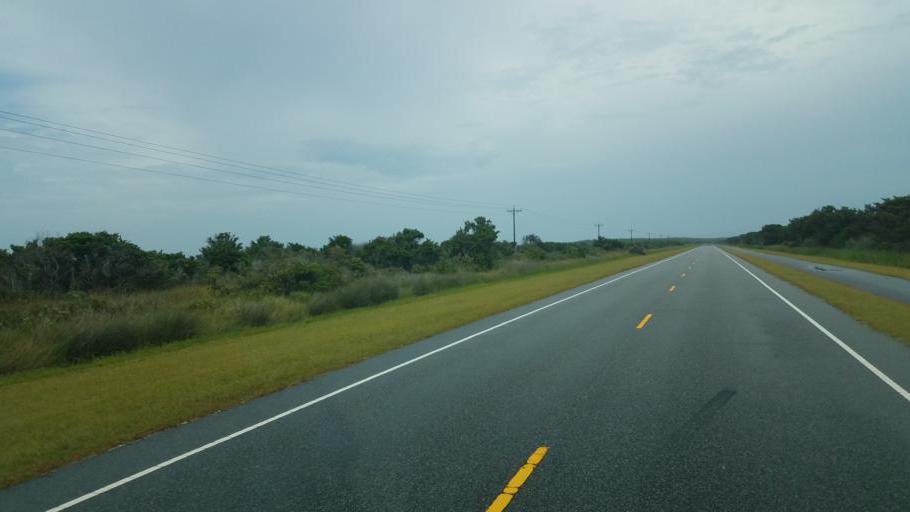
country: US
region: North Carolina
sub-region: Dare County
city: Buxton
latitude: 35.1183
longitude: -75.9368
